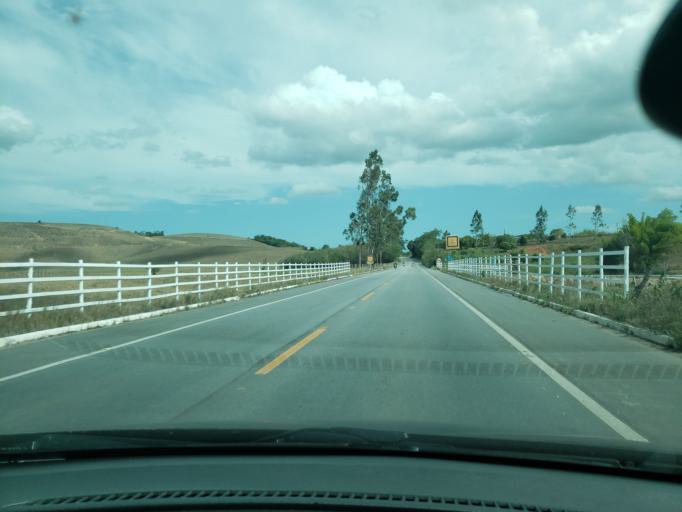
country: BR
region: Alagoas
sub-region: Murici
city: Murici
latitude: -9.3231
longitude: -35.9248
